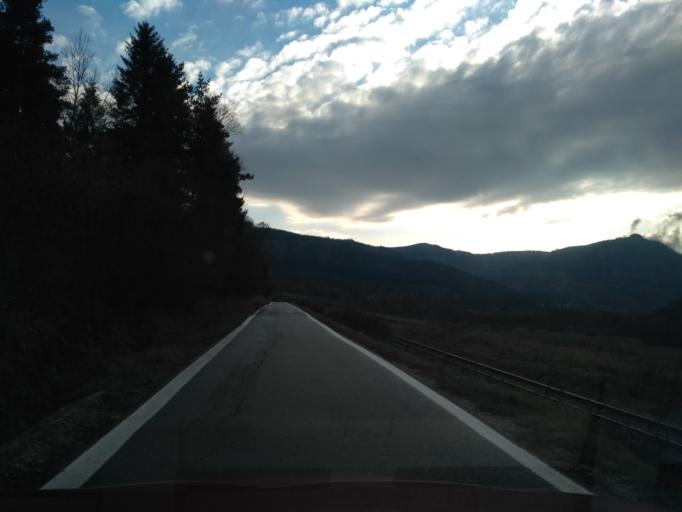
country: SK
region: Kosicky
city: Spisska Nova Ves
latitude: 48.8283
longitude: 20.6035
